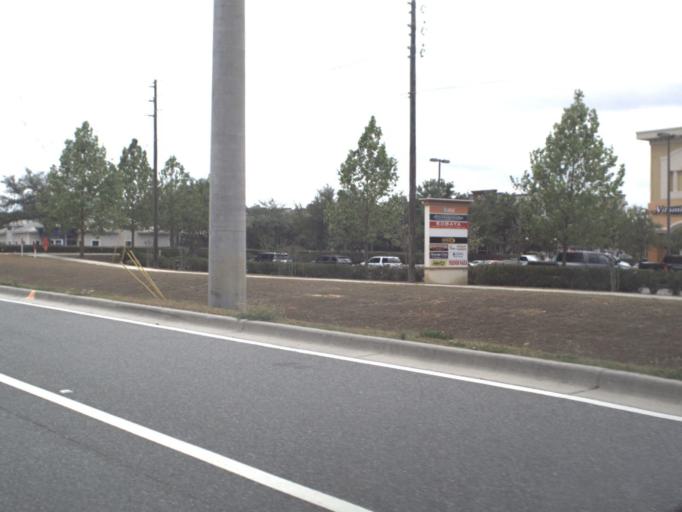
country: US
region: Florida
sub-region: Lake County
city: Minneola
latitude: 28.5465
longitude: -81.7286
